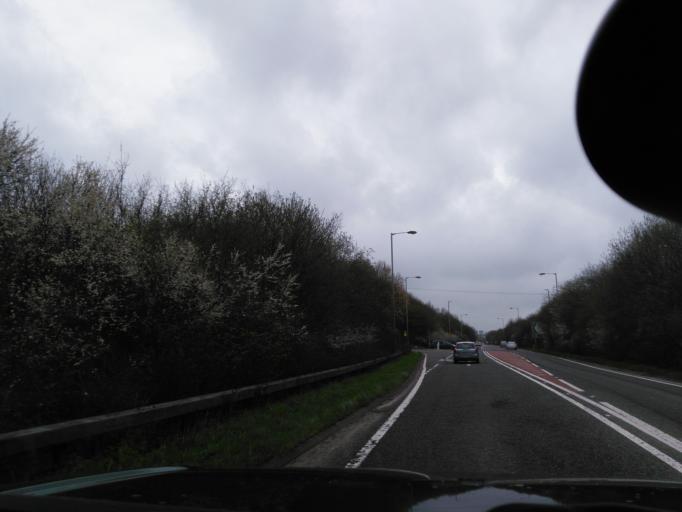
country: GB
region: England
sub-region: Somerset
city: Frome
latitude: 51.2255
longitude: -2.3010
